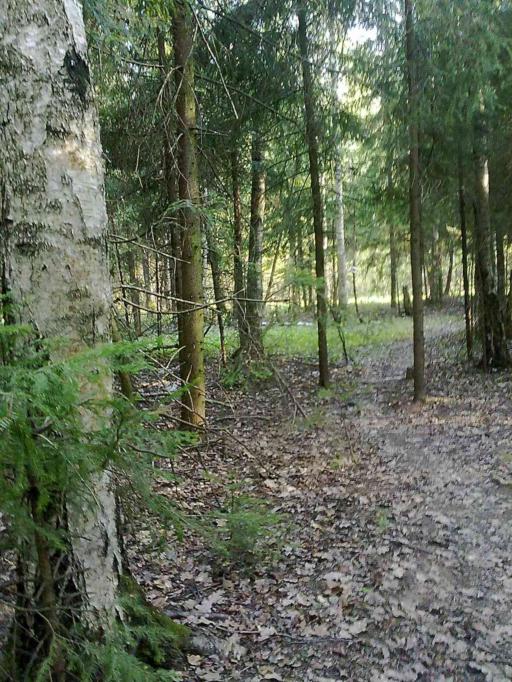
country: RU
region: Moscow
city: Tolstopal'tsevo
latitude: 55.6092
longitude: 37.2403
